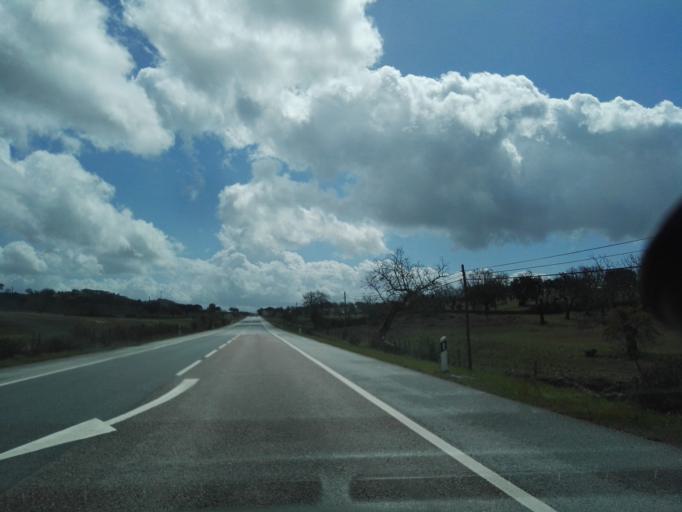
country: PT
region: Portalegre
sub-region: Portalegre
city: Urra
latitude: 39.2463
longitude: -7.4008
